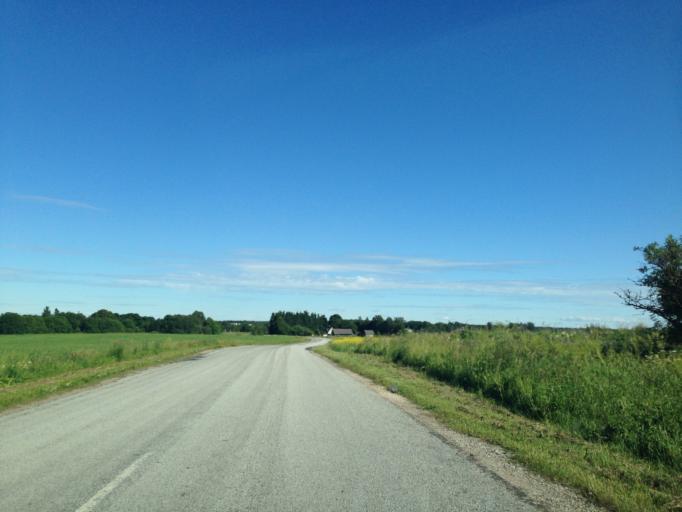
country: EE
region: Harju
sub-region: Kuusalu vald
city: Kuusalu
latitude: 59.4536
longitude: 25.3675
